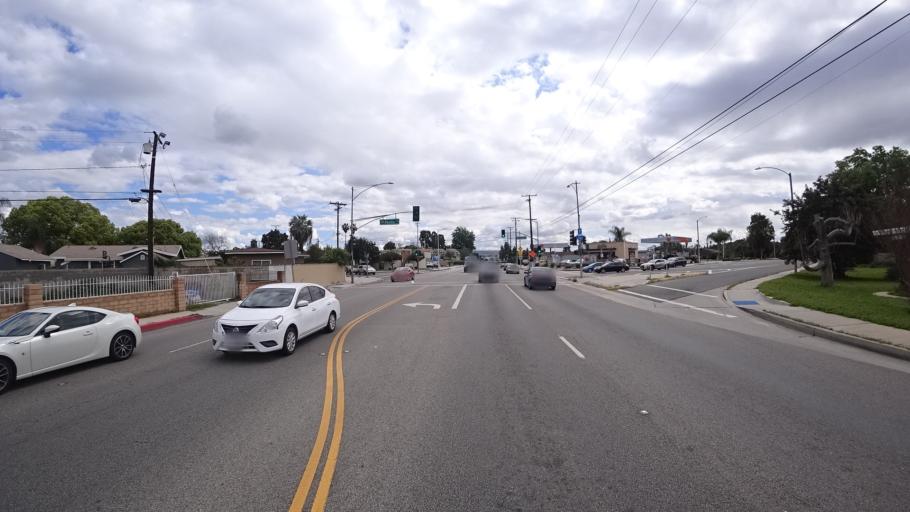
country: US
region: California
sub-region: Los Angeles County
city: West Covina
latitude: 34.0750
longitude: -117.9466
